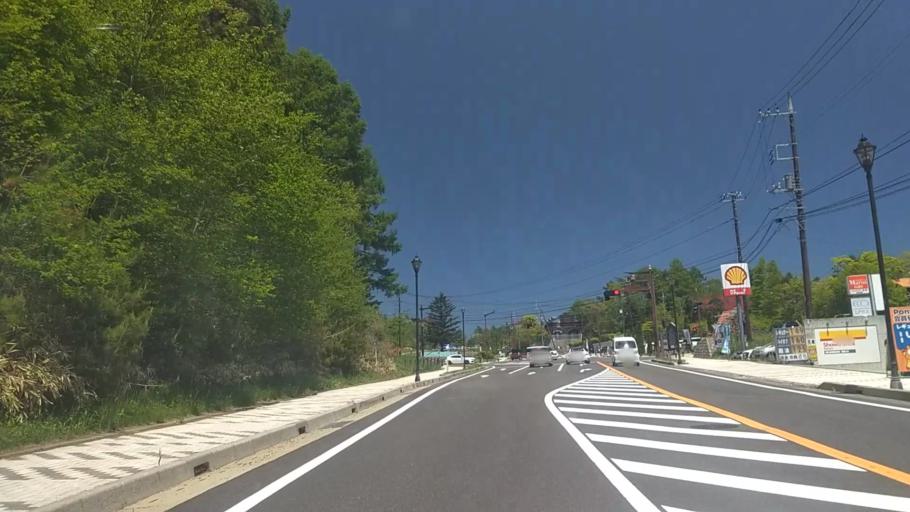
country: JP
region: Yamanashi
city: Nirasaki
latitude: 35.9145
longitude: 138.4418
